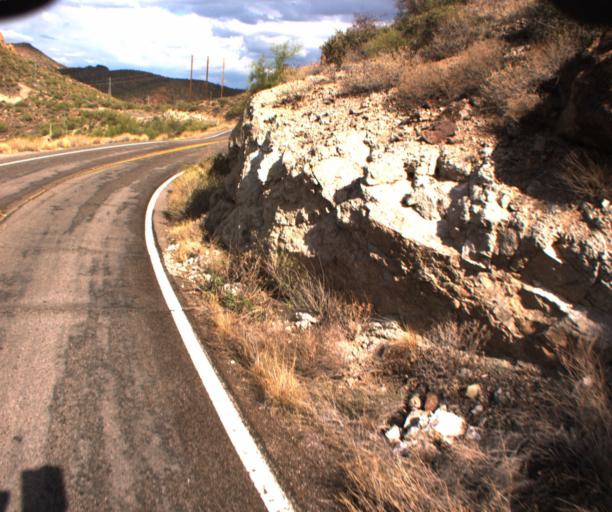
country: US
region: Arizona
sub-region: Pinal County
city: Apache Junction
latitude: 33.5106
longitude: -111.4557
